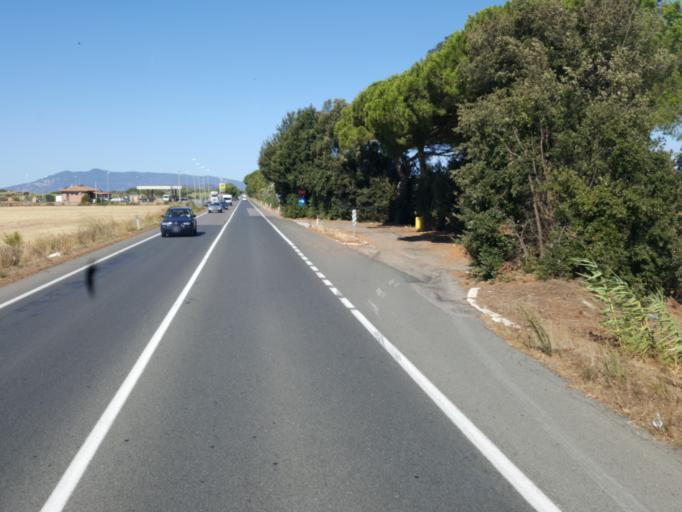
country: IT
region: Tuscany
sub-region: Provincia di Grosseto
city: Capalbio
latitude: 42.4151
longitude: 11.3685
